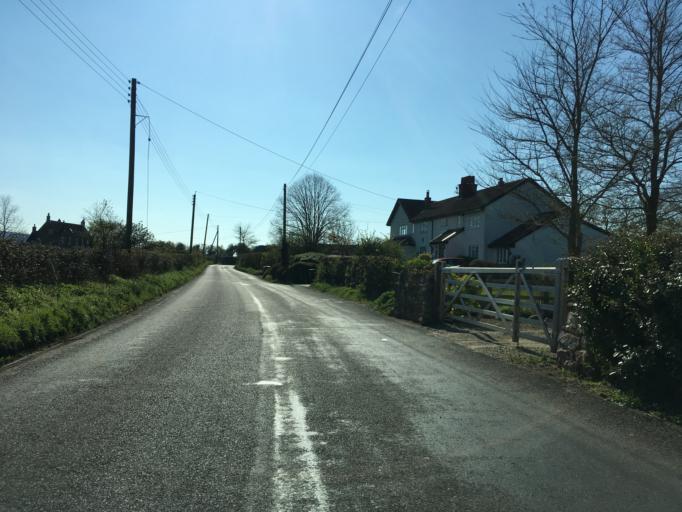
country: GB
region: England
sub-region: North Somerset
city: Portishead
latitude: 51.4821
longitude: -2.7391
